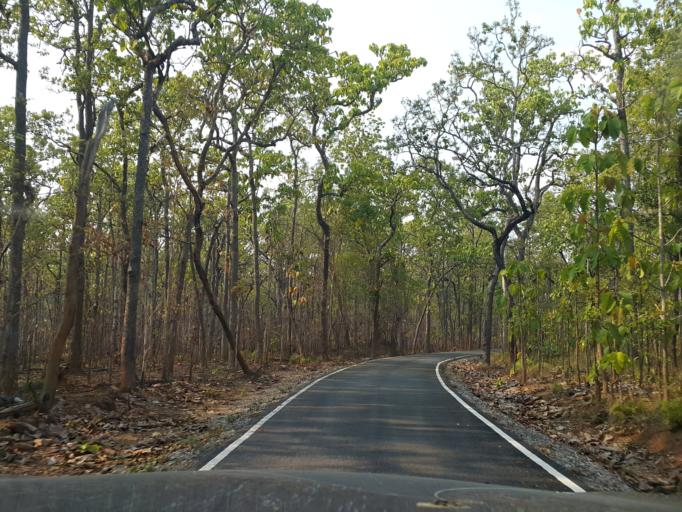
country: TH
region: Lamphun
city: Li
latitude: 17.6241
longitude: 98.8708
